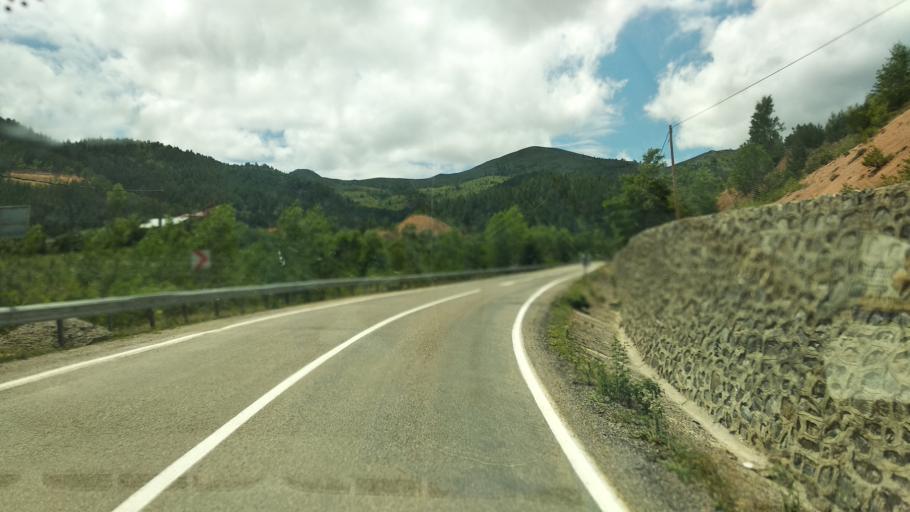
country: TR
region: Gumushane
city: Kose
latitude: 40.3041
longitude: 39.5569
